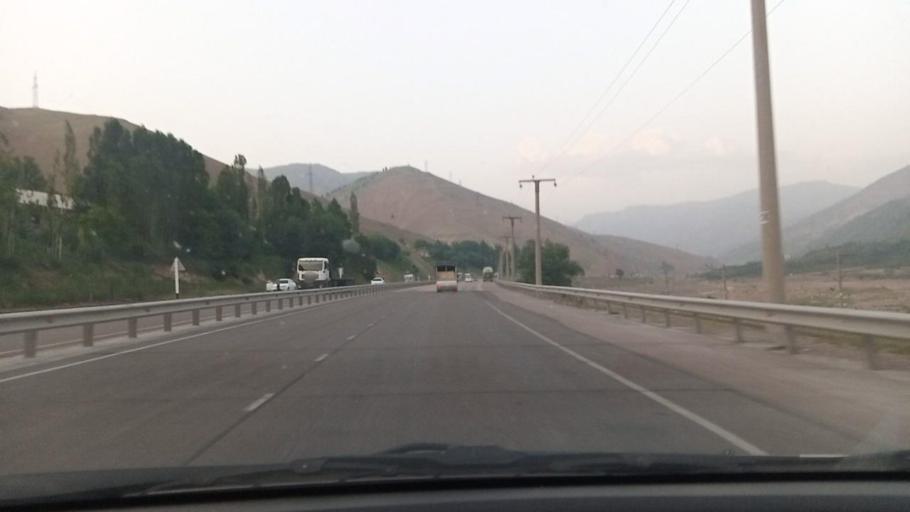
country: UZ
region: Toshkent
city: Angren
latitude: 41.1425
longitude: 70.4030
